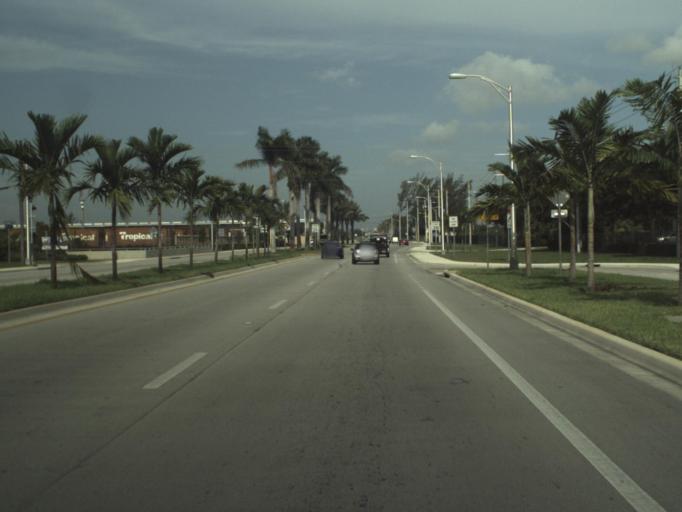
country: US
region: Florida
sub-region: Palm Beach County
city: Mangonia Park
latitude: 26.7697
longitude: -80.0746
